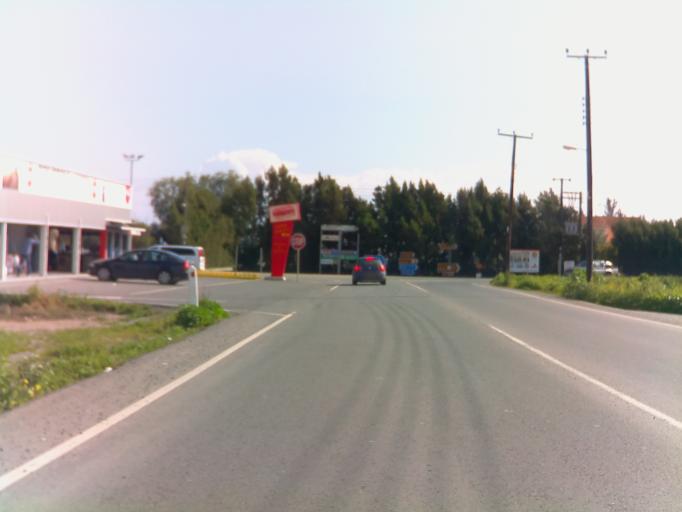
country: CY
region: Larnaka
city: Meneou
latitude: 34.8672
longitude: 33.5985
